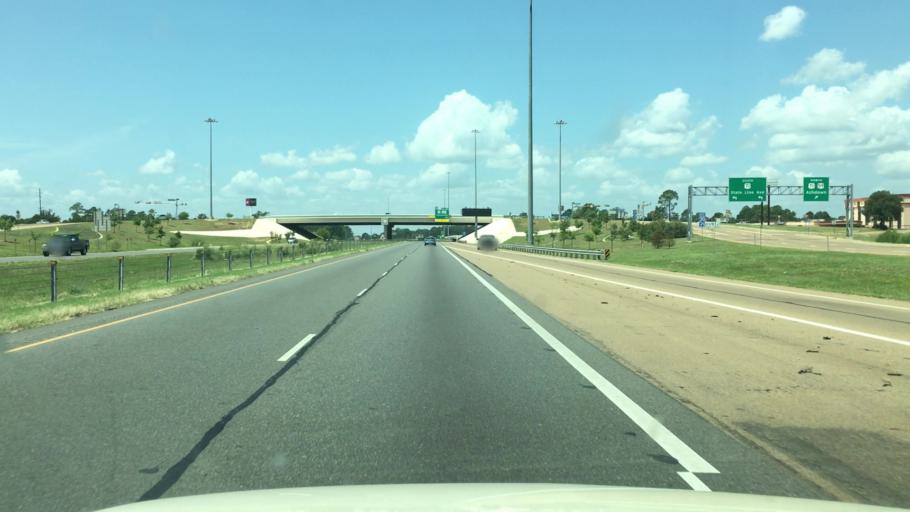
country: US
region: Arkansas
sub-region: Miller County
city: Texarkana
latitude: 33.4704
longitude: -94.0397
